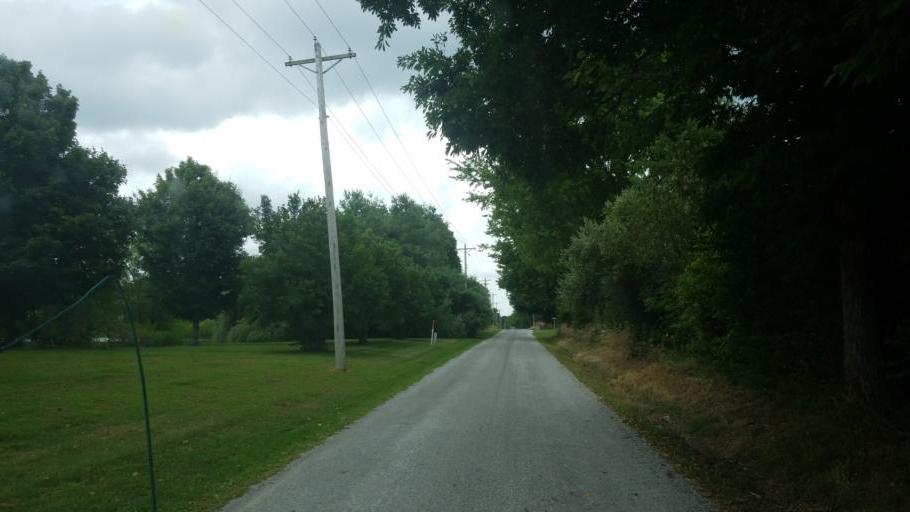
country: US
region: Illinois
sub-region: Jackson County
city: Murphysboro
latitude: 37.7122
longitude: -89.3270
